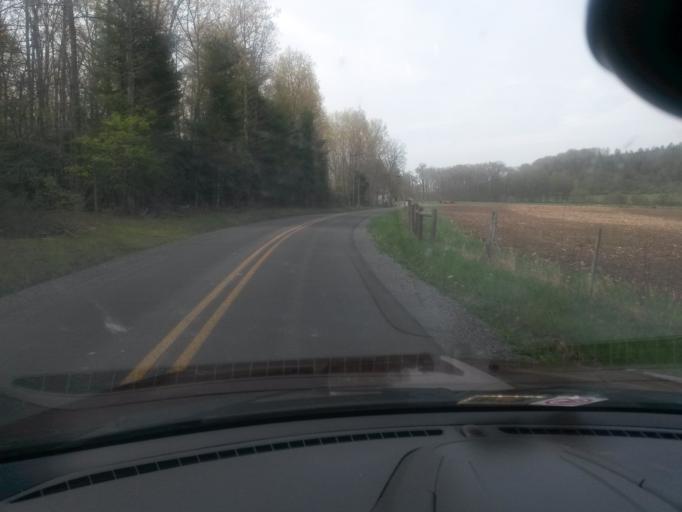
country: US
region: West Virginia
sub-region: Pocahontas County
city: Marlinton
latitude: 38.0947
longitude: -80.2257
